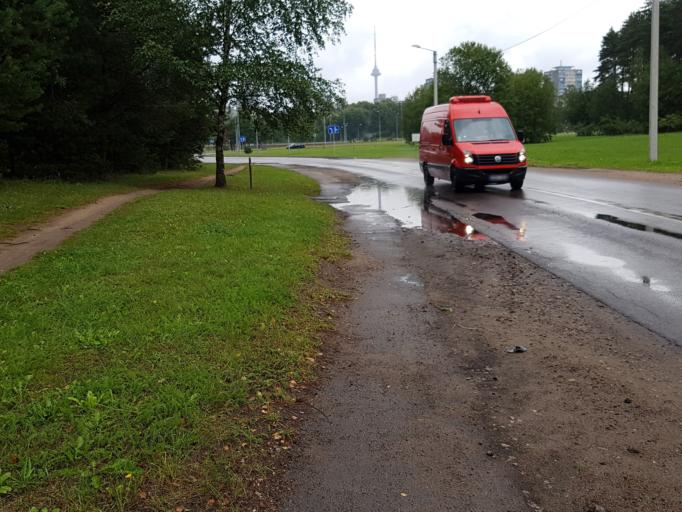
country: LT
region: Vilnius County
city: Lazdynai
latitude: 54.6687
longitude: 25.1976
